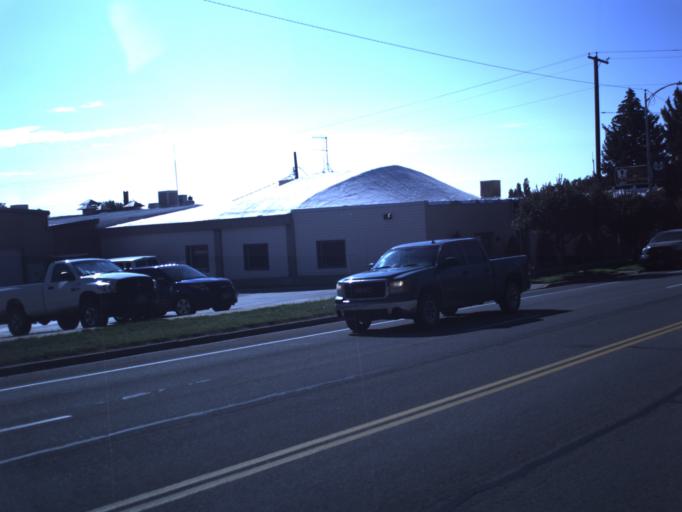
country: US
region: Utah
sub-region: San Juan County
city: Blanding
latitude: 37.6209
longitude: -109.4781
